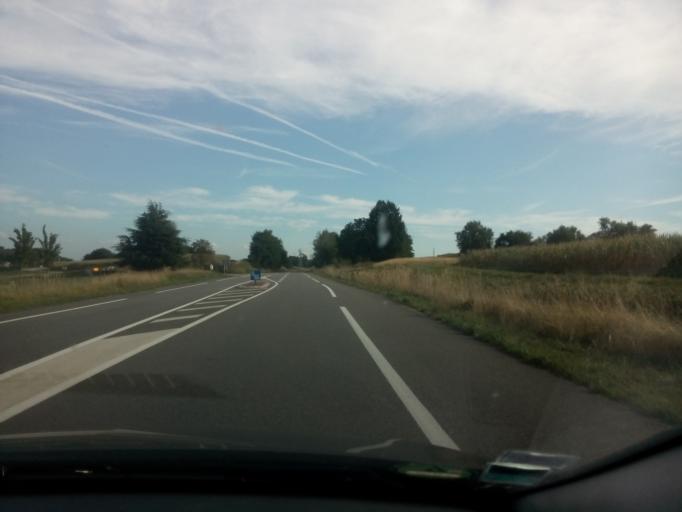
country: FR
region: Alsace
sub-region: Departement du Bas-Rhin
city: Wissembourg
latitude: 49.0165
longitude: 7.9685
